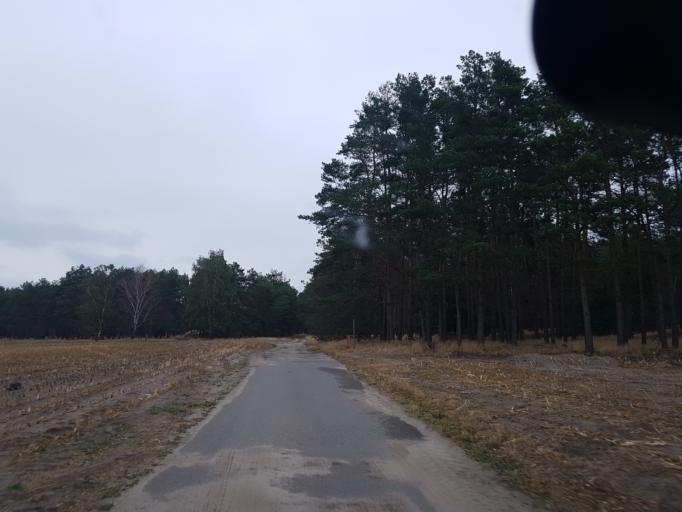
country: DE
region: Brandenburg
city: Schilda
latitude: 51.6412
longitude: 13.3292
